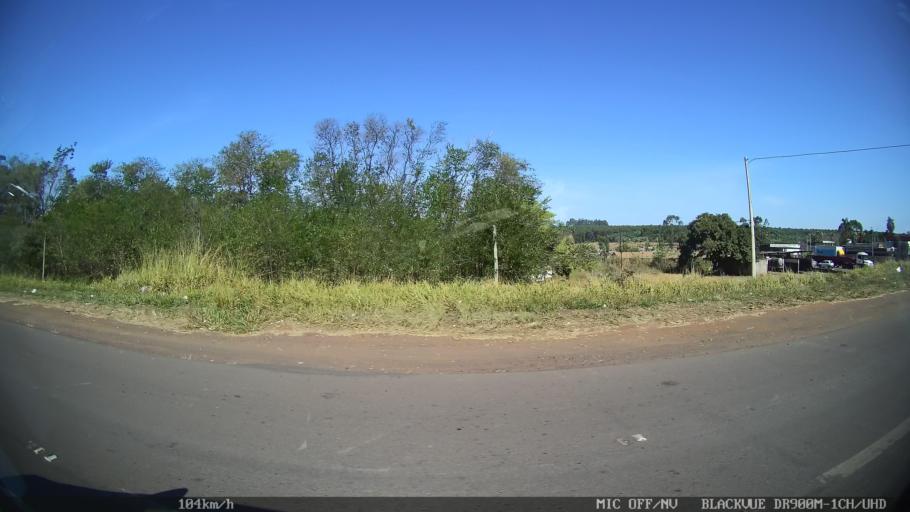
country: BR
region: Sao Paulo
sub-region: Batatais
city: Batatais
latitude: -20.9059
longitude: -47.5986
